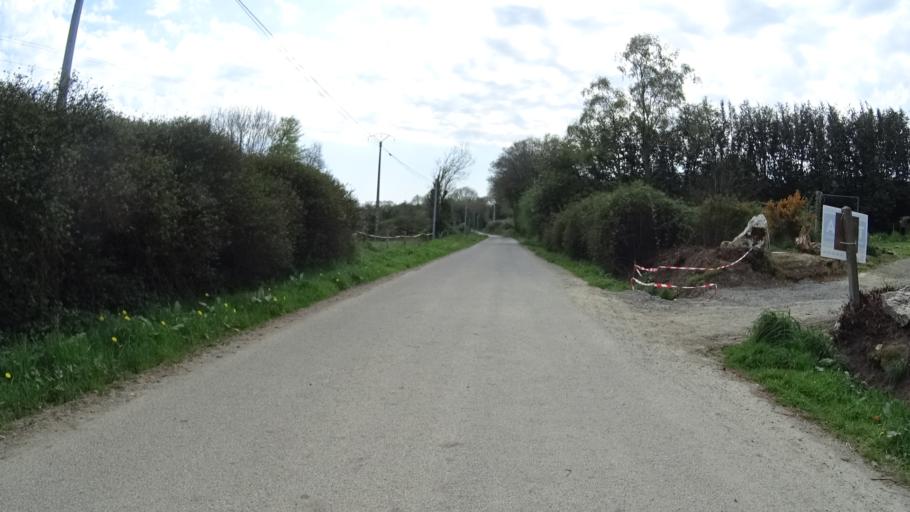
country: FR
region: Brittany
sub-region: Departement du Finistere
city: Sizun
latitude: 48.4201
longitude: -4.0554
